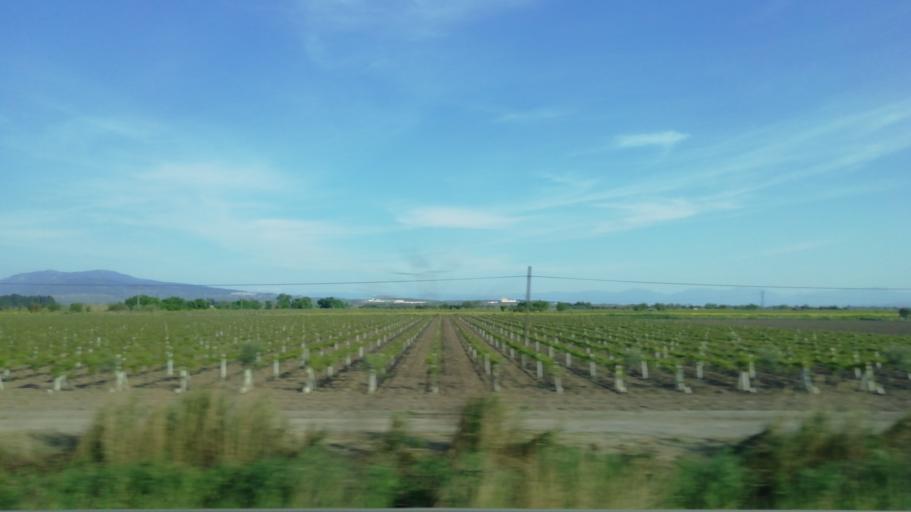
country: TR
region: Manisa
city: Saruhanli
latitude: 38.7236
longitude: 27.5678
